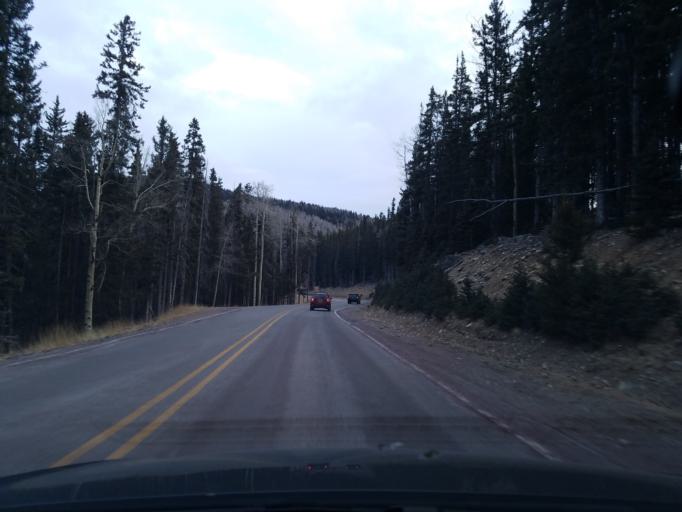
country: US
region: New Mexico
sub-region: Santa Fe County
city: Santa Fe
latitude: 35.7918
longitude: -105.8039
